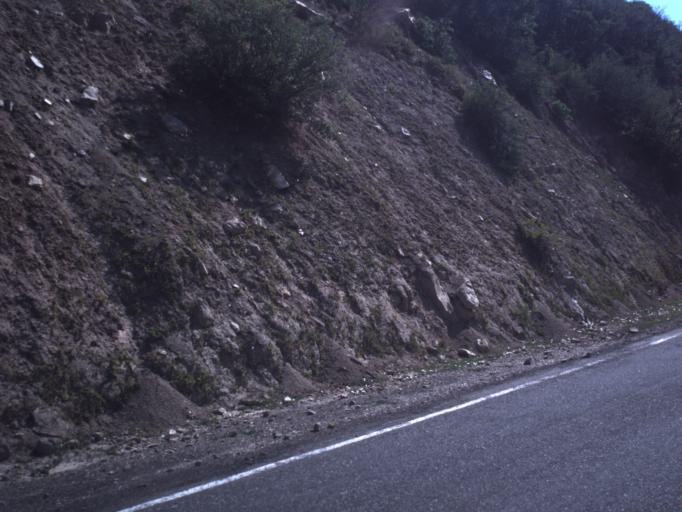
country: US
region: Utah
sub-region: Sanpete County
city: Fairview
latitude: 39.6488
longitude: -111.3840
